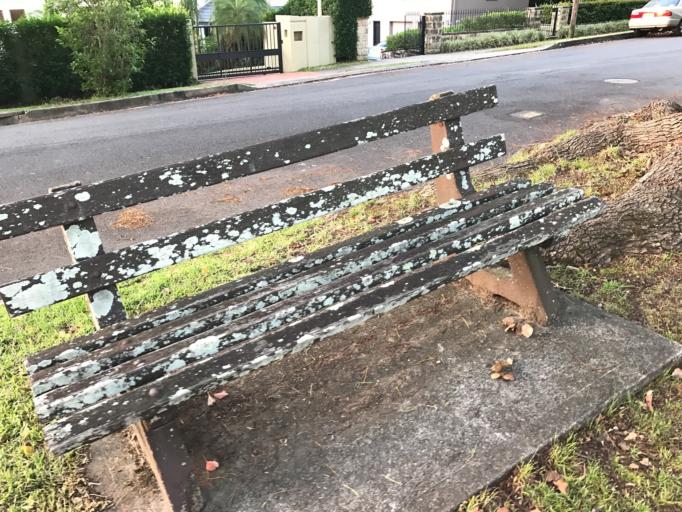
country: AU
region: New South Wales
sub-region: Ku-ring-gai
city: Killara
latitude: -33.7626
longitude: 151.1671
